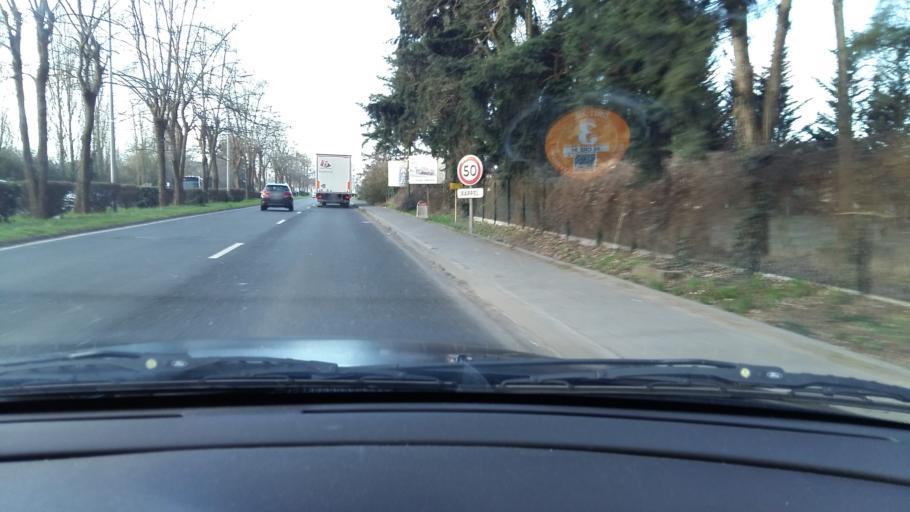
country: FR
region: Ile-de-France
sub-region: Departement de l'Essonne
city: Fleury-Merogis
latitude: 48.6444
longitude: 2.3645
